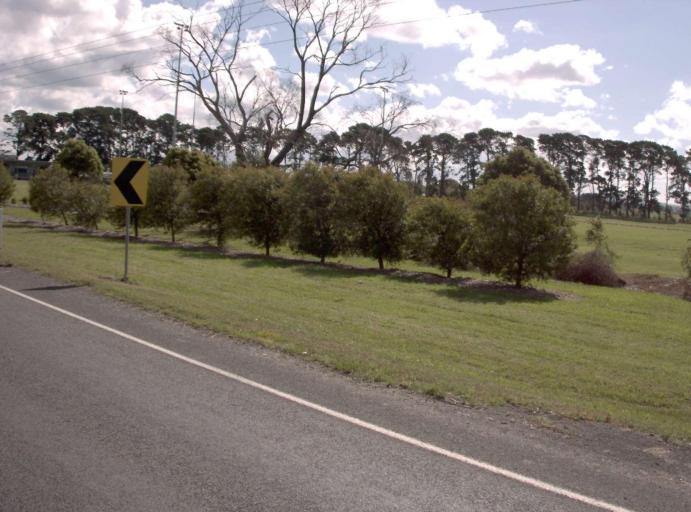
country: AU
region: Victoria
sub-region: Latrobe
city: Morwell
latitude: -38.2958
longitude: 146.4232
